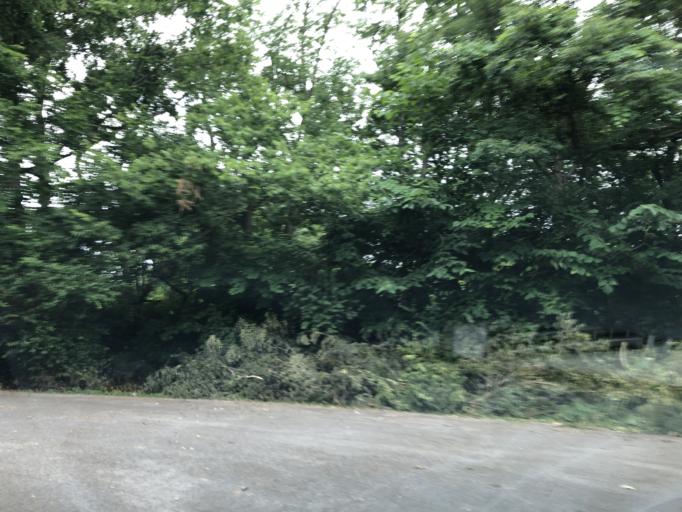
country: US
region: Tennessee
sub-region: Davidson County
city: Goodlettsville
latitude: 36.2871
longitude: -86.7378
